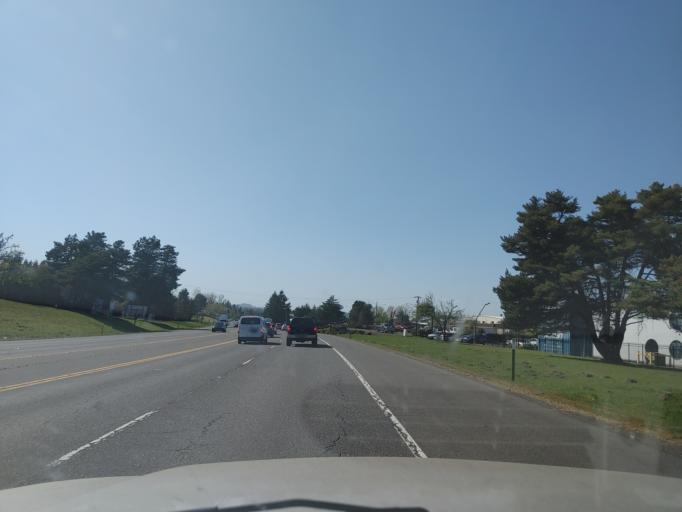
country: US
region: Oregon
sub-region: Clackamas County
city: Oatfield
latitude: 45.4238
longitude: -122.5866
